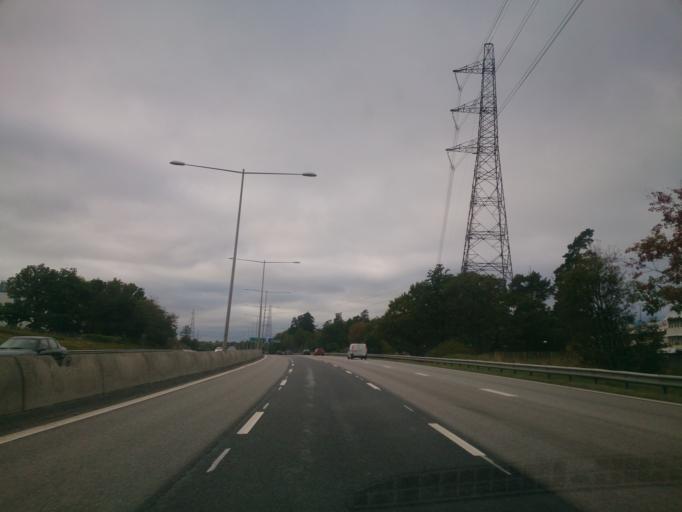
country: SE
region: Stockholm
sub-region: Huddinge Kommun
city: Segeltorp
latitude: 59.2811
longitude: 17.9225
